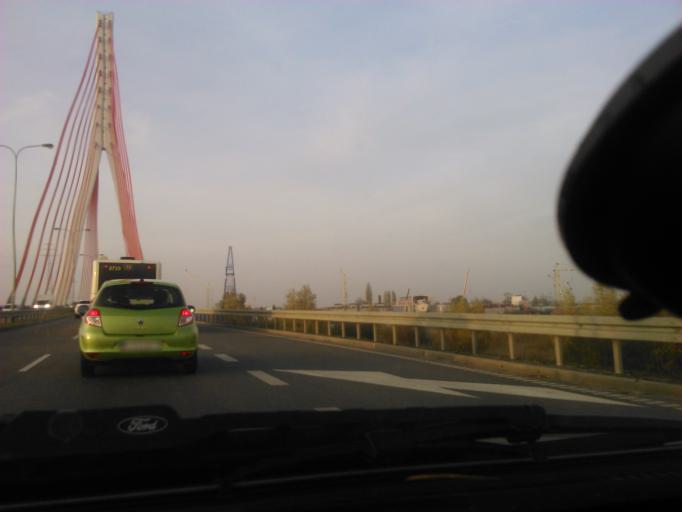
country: PL
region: Pomeranian Voivodeship
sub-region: Gdansk
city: Gdansk
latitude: 54.3536
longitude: 18.6959
